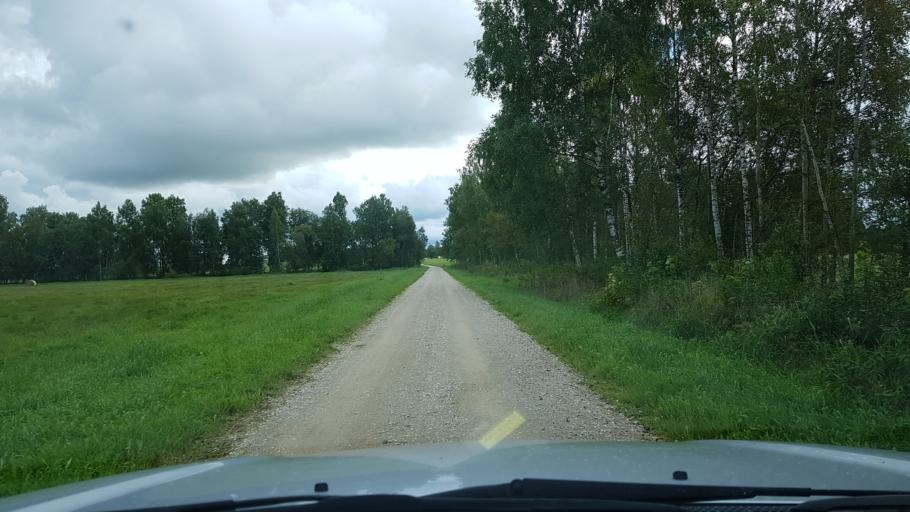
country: EE
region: Harju
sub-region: Rae vald
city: Vaida
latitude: 59.2697
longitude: 25.0495
